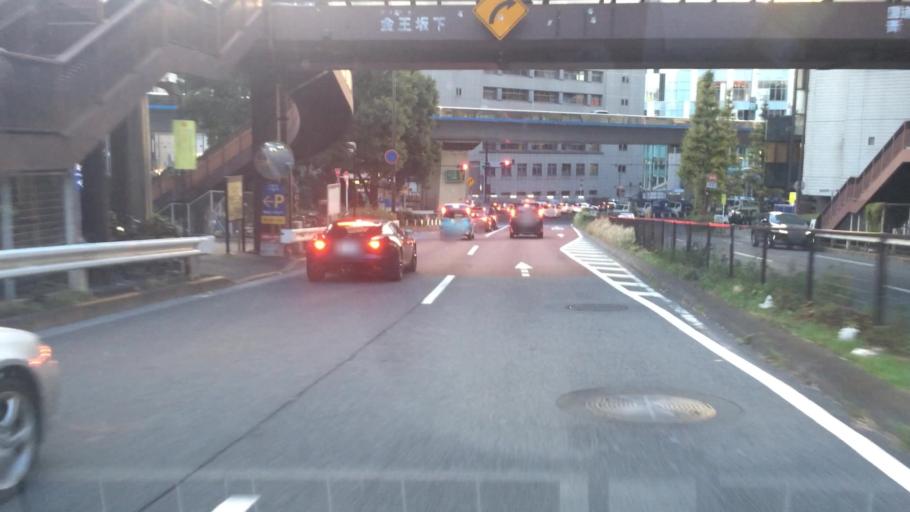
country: JP
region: Tokyo
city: Tokyo
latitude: 35.6589
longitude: 139.7049
